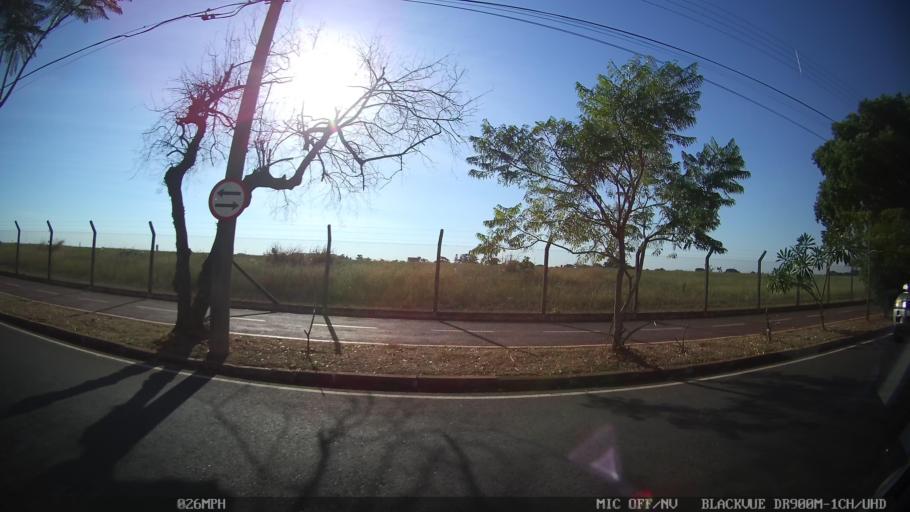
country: BR
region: Sao Paulo
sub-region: Sao Jose Do Rio Preto
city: Sao Jose do Rio Preto
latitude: -20.8206
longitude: -49.4093
